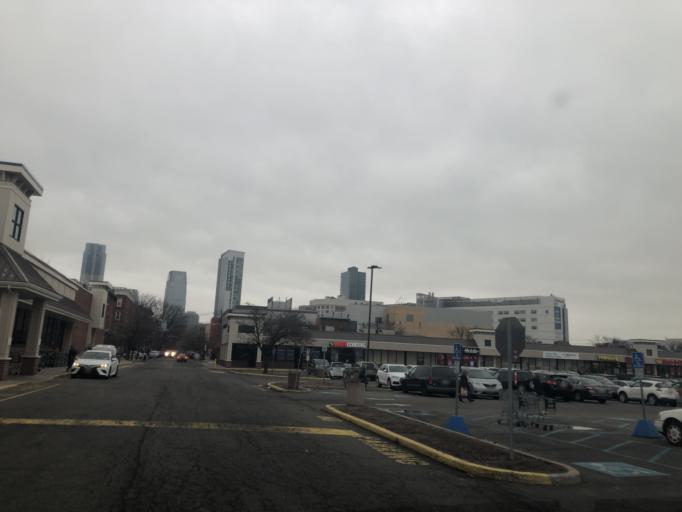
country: US
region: New Jersey
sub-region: Hudson County
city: Jersey City
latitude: 40.7189
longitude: -74.0529
